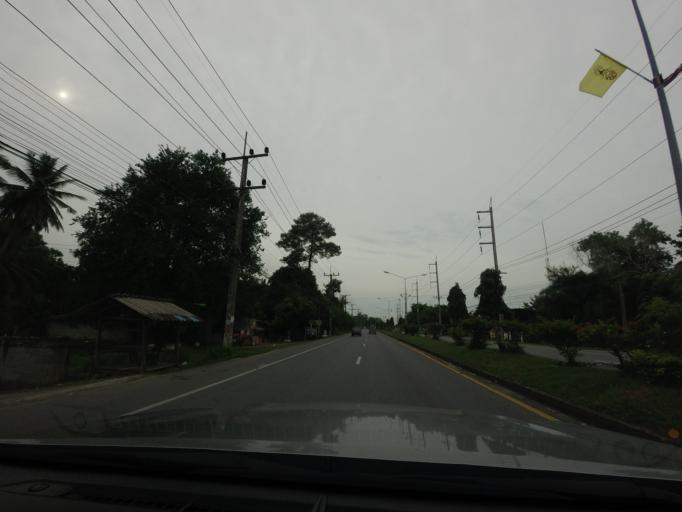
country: TH
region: Songkhla
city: Sathing Phra
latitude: 7.5160
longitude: 100.4258
